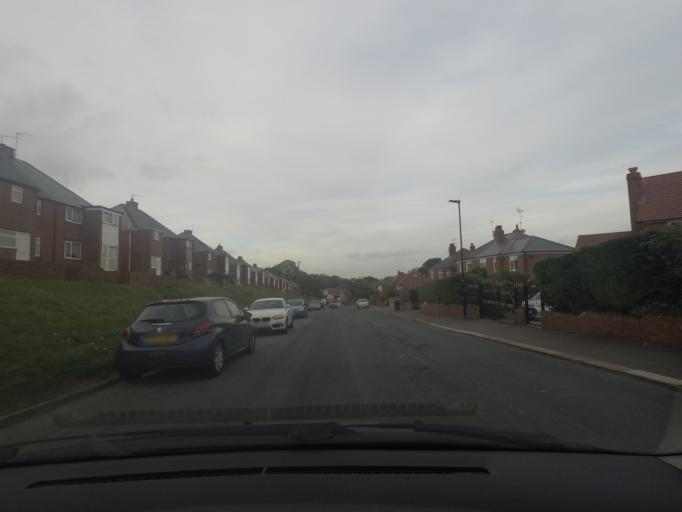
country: GB
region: England
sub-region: Sheffield
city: Chapletown
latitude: 53.4390
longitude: -1.4981
